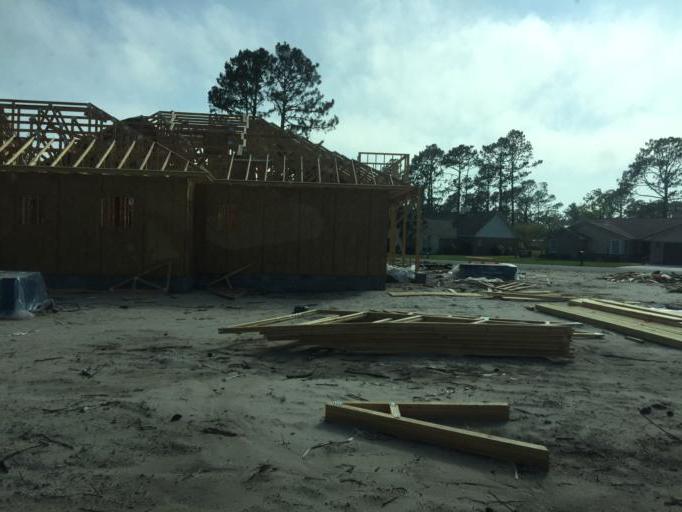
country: US
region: Florida
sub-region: Bay County
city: Panama City Beach
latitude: 30.2148
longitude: -85.8414
